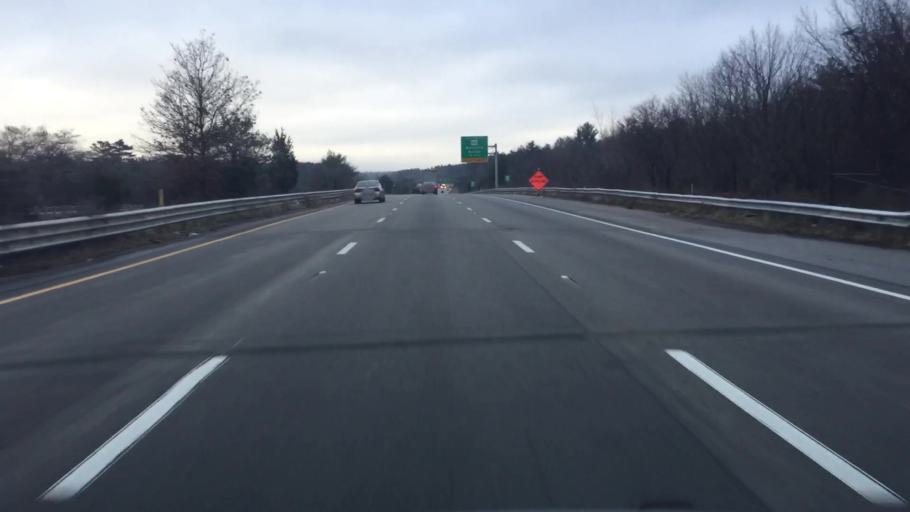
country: US
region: Massachusetts
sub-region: Bristol County
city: Mansfield Center
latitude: 42.0120
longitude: -71.2328
